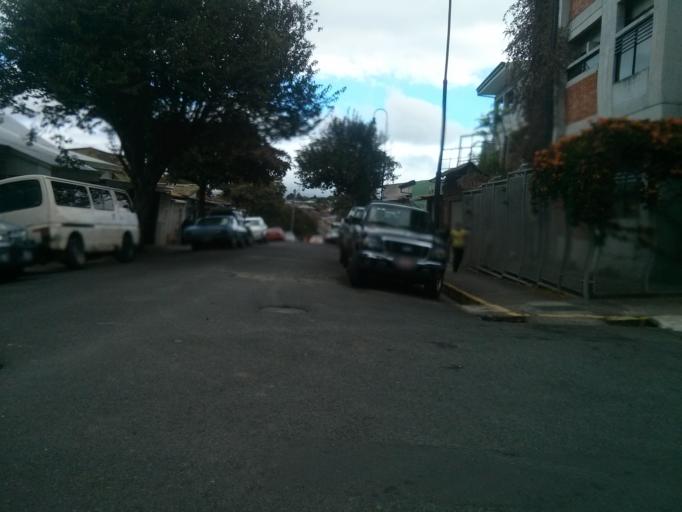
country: CR
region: San Jose
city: Calle Blancos
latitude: 9.9389
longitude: -84.0679
